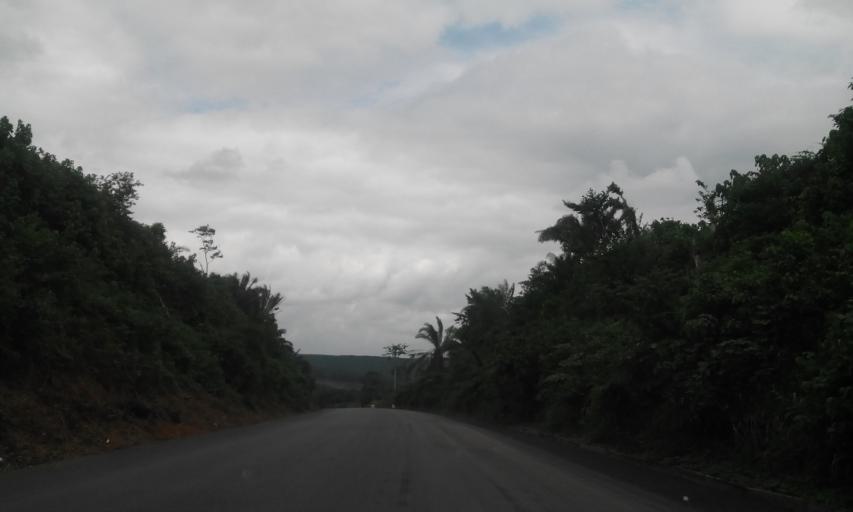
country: CI
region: Sud-Comoe
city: Mafere
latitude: 5.3146
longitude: -3.0509
